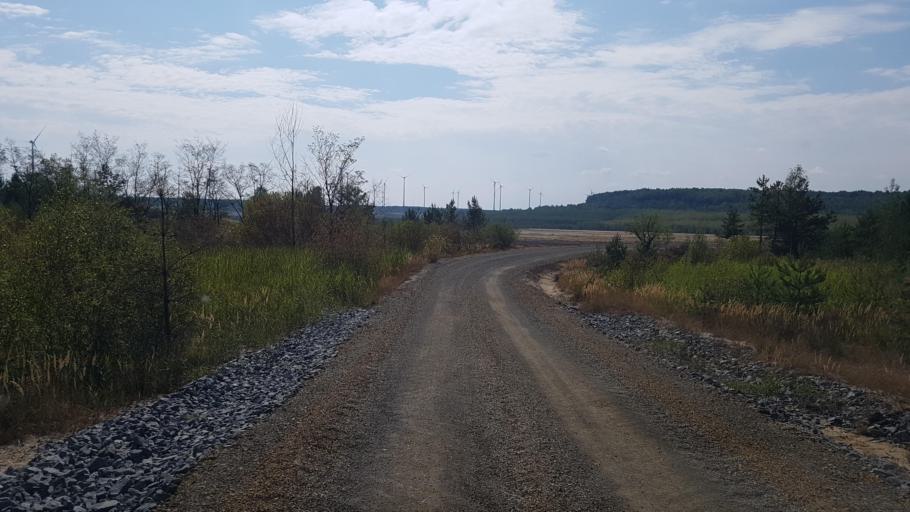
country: DE
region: Brandenburg
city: Sallgast
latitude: 51.5499
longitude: 13.8419
